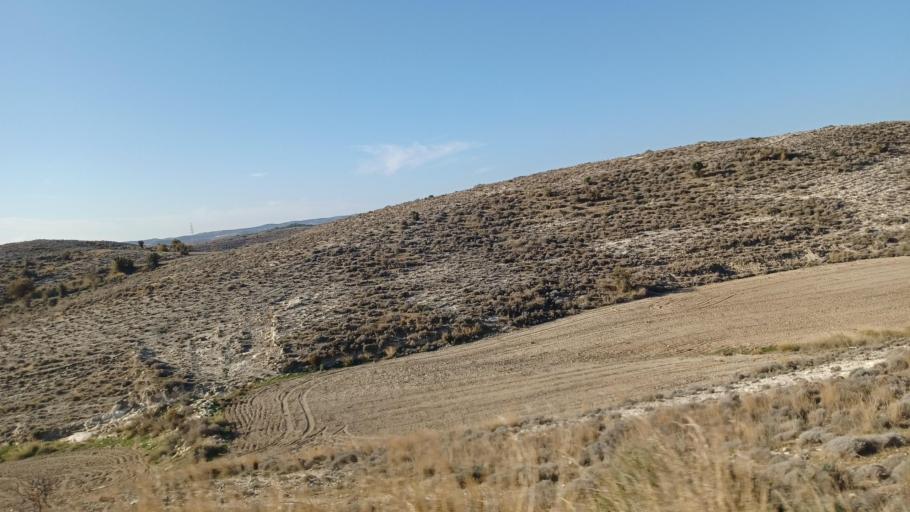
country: CY
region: Larnaka
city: Psevdas
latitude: 34.9416
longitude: 33.5207
